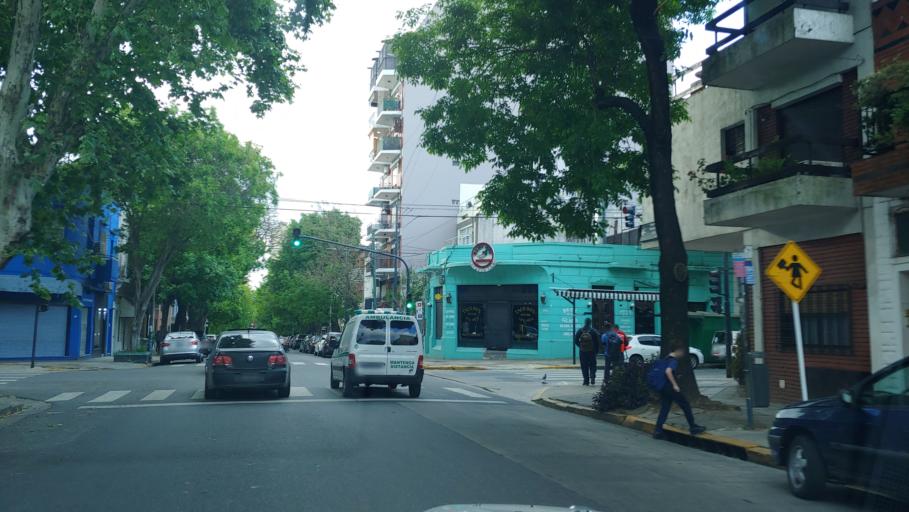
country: AR
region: Buenos Aires F.D.
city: Colegiales
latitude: -34.5741
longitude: -58.4549
